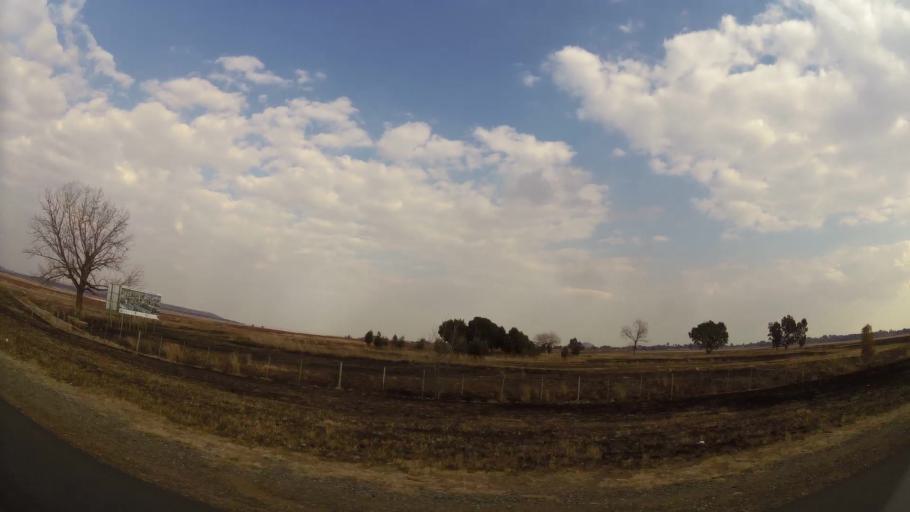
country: ZA
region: Gauteng
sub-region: Ekurhuleni Metropolitan Municipality
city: Springs
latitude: -26.2692
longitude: 28.4895
